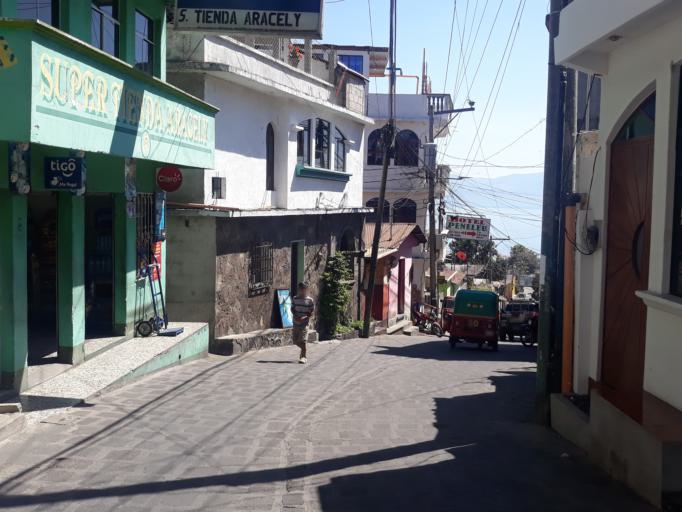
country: GT
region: Solola
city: San Pedro La Laguna
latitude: 14.6924
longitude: -91.2707
